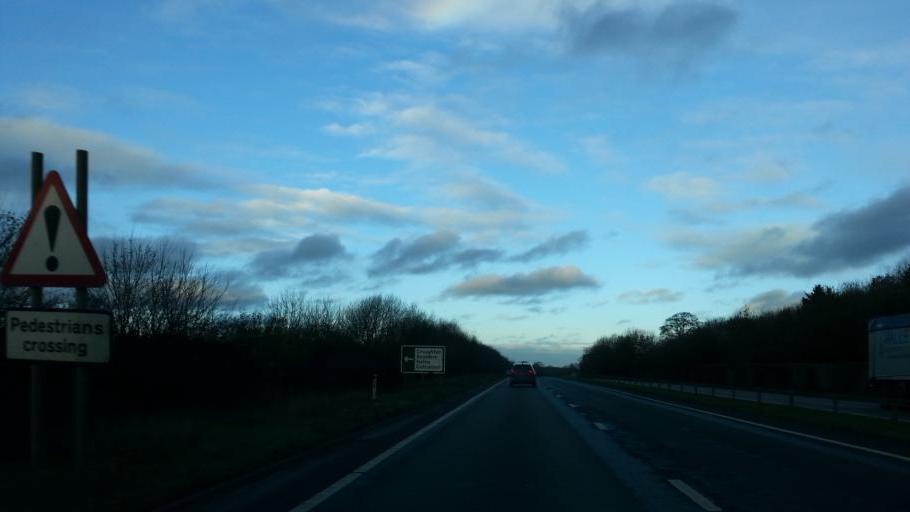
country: GB
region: England
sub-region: Oxfordshire
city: Bicester
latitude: 51.9676
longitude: -1.1960
